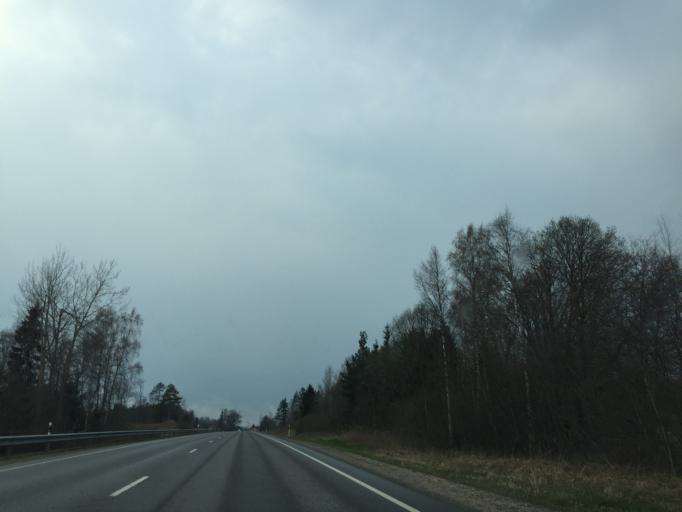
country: EE
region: Tartu
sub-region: UElenurme vald
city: Ulenurme
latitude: 58.1408
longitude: 26.7088
